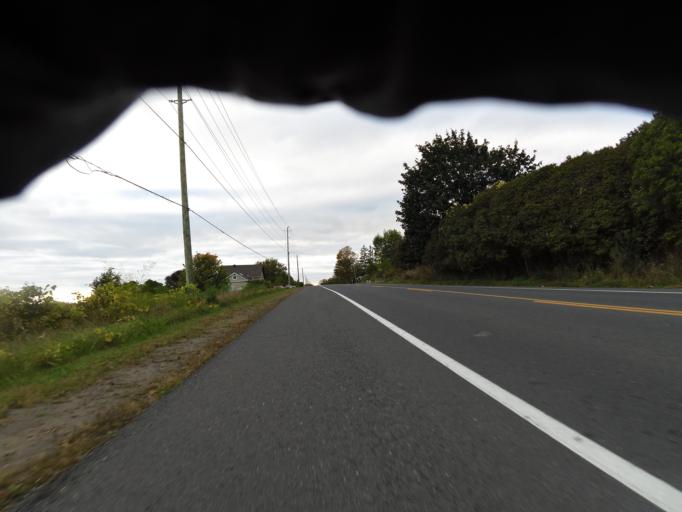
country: CA
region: Ontario
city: Cobourg
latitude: 44.0130
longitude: -77.8558
